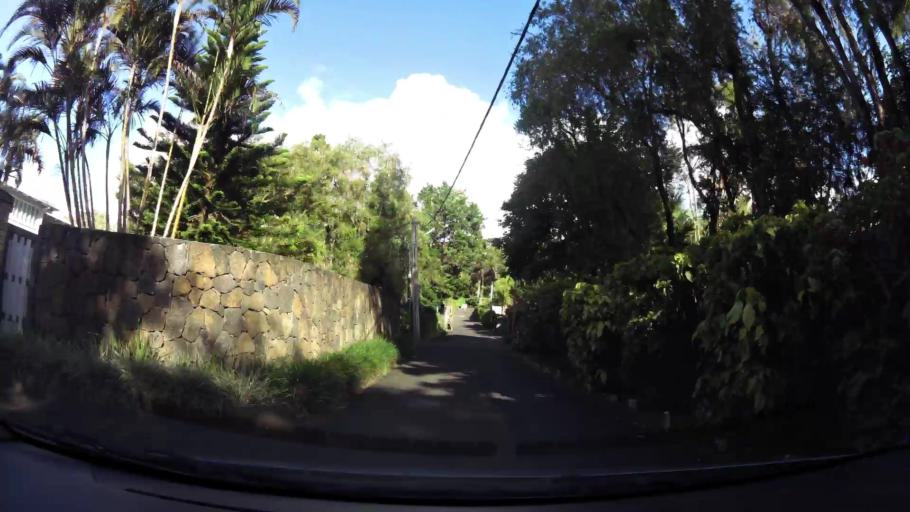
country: MU
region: Plaines Wilhems
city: Curepipe
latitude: -20.3128
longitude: 57.5028
